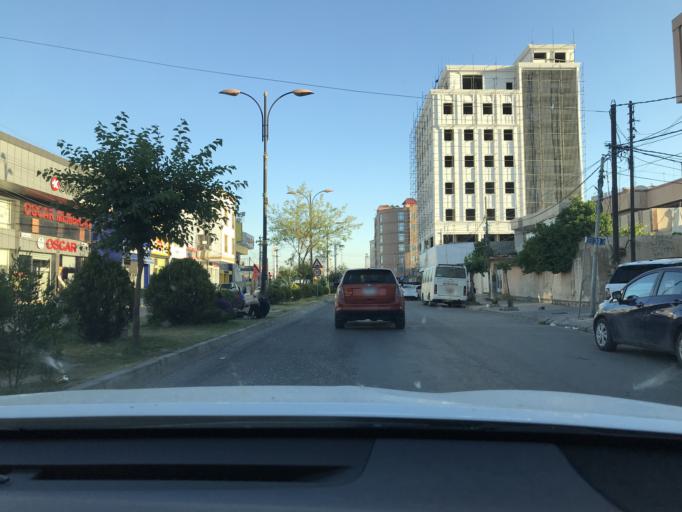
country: IQ
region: Arbil
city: Erbil
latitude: 36.2052
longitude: 44.0099
